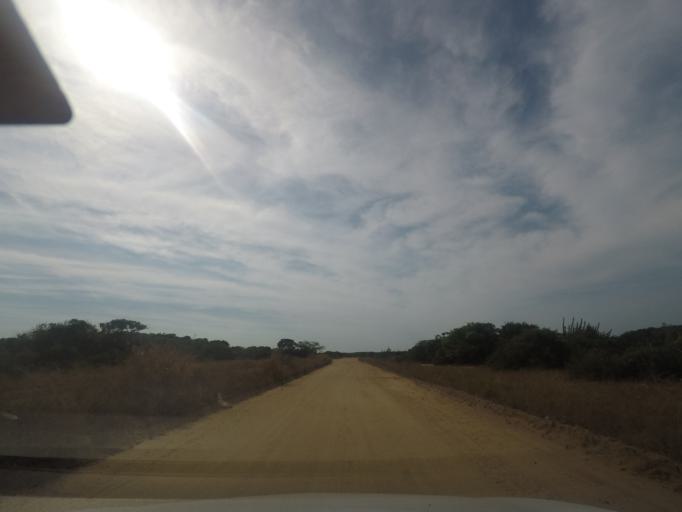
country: BR
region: Rio de Janeiro
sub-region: Marica
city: Marica
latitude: -22.9488
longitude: -42.8872
